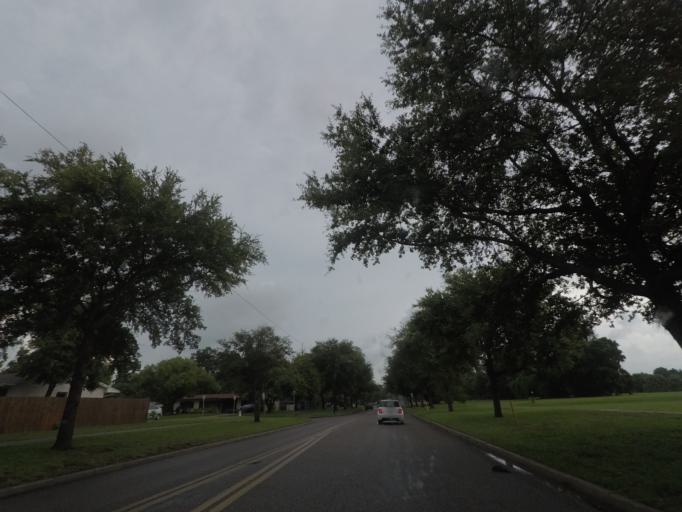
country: US
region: Florida
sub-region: Pinellas County
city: Kenneth City
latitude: 27.7919
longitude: -82.7411
